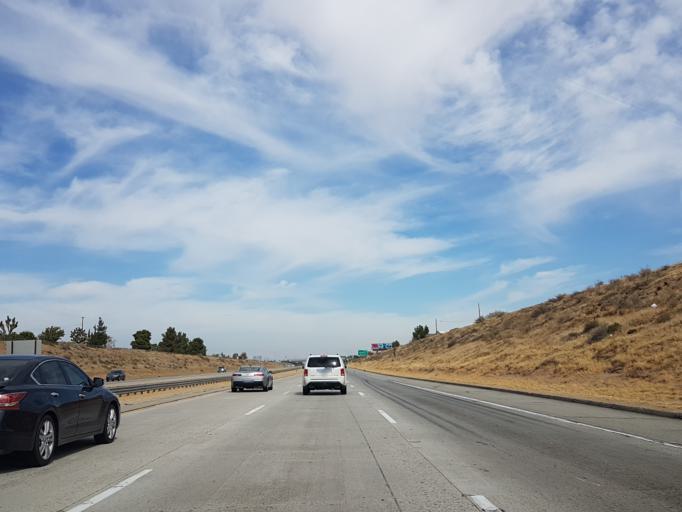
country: US
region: California
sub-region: Los Angeles County
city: Lancaster
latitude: 34.6510
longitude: -118.1531
